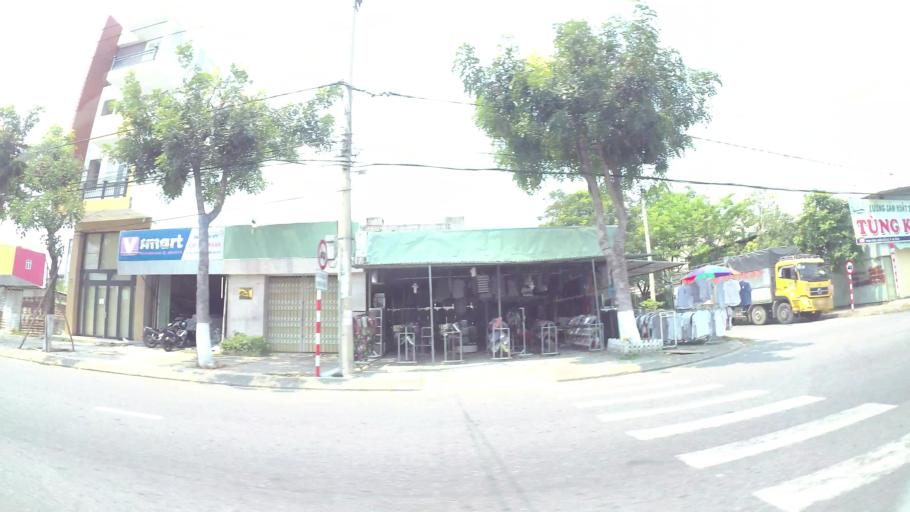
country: VN
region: Da Nang
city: Cam Le
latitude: 15.9873
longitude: 108.2078
